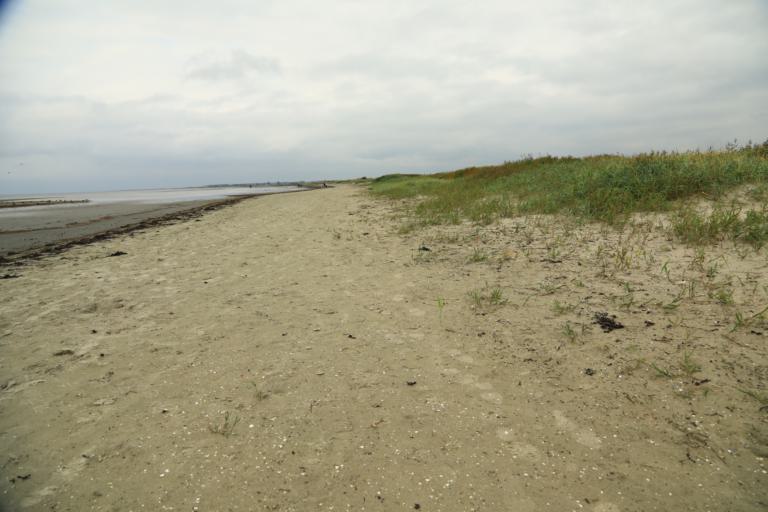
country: SE
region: Halland
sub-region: Varbergs Kommun
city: Tvaaker
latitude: 57.0043
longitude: 12.3513
